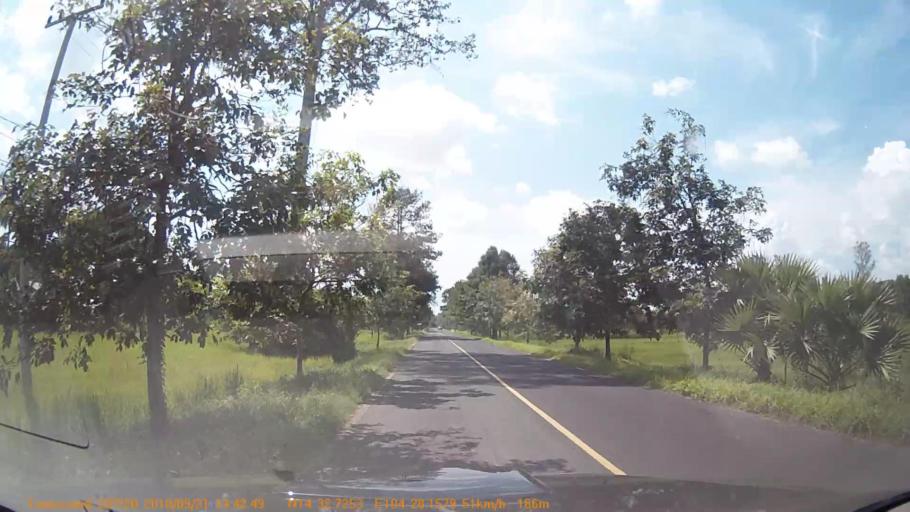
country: TH
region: Sisaket
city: Khun Han
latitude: 14.5456
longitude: 104.4689
